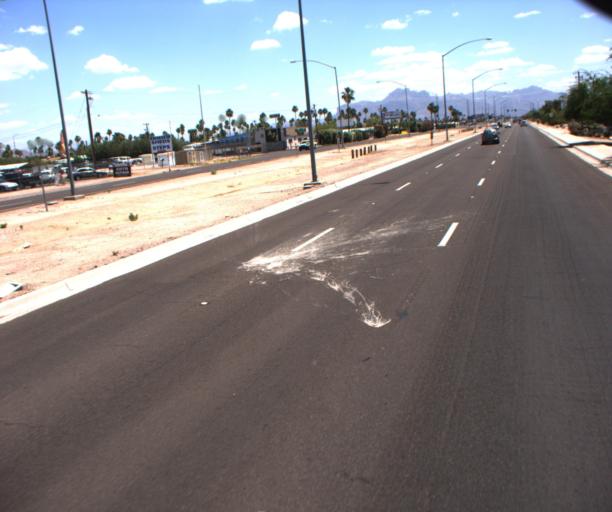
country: US
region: Arizona
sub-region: Pinal County
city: Apache Junction
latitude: 33.4151
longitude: -111.6066
